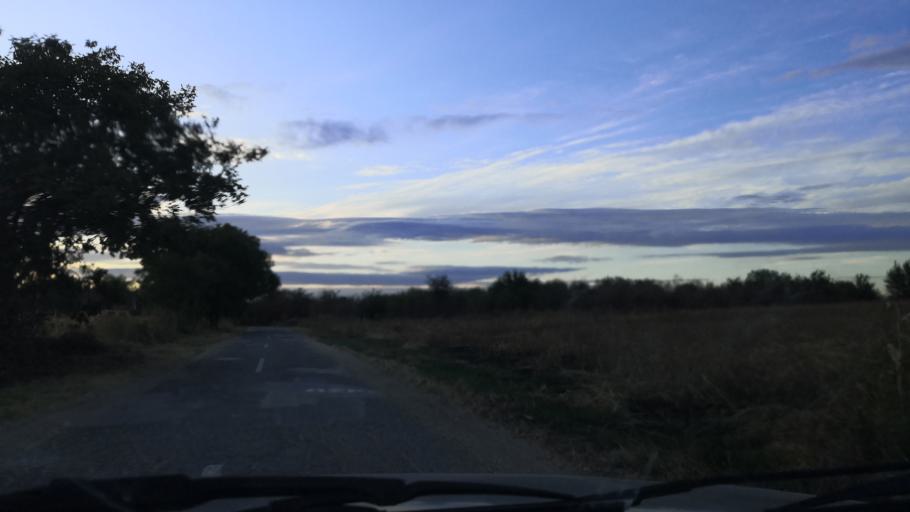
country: RO
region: Mehedinti
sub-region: Comuna Gruia
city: Izvoarele
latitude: 44.2739
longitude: 22.6636
